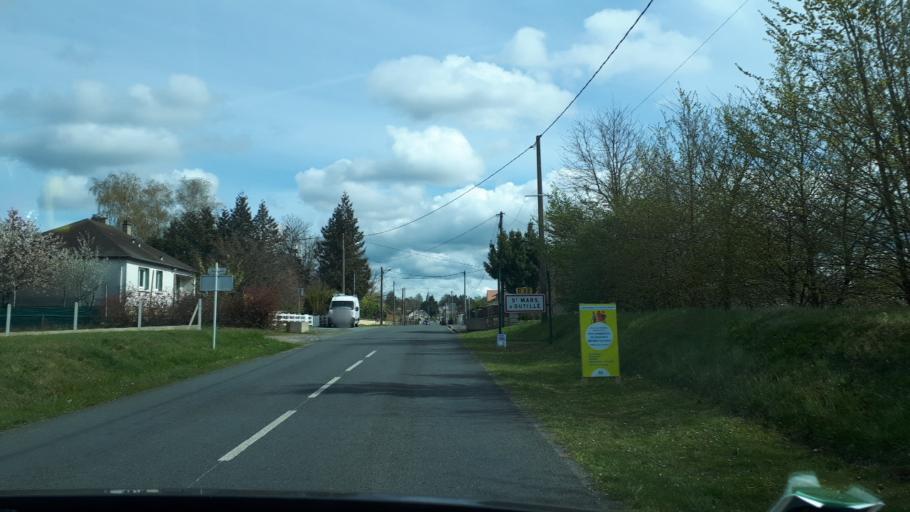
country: FR
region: Pays de la Loire
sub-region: Departement de la Sarthe
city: Brette-les-Pins
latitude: 47.8664
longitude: 0.3247
